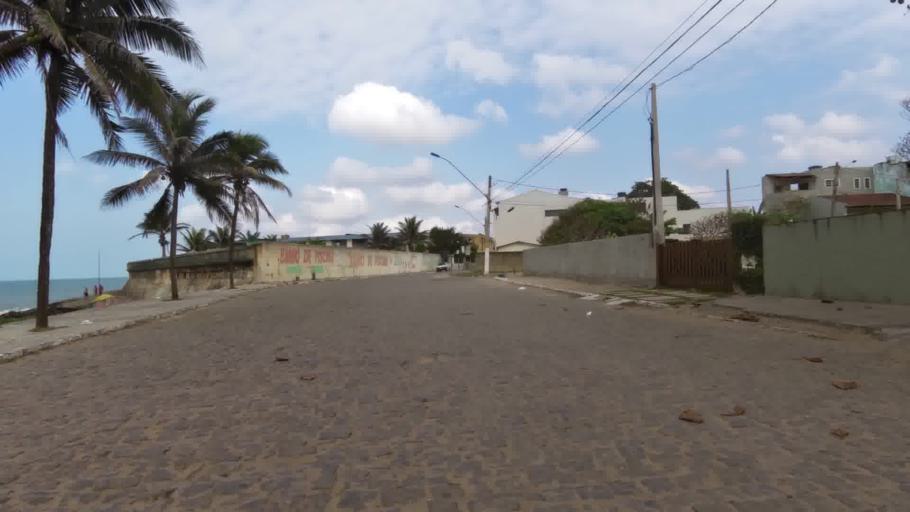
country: BR
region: Espirito Santo
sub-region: Marataizes
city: Marataizes
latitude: -21.0418
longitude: -40.8220
